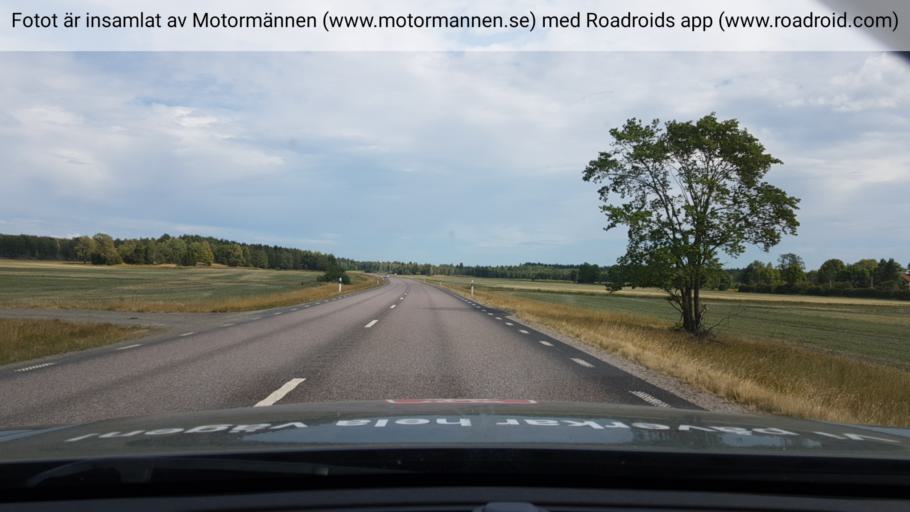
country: SE
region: Uppsala
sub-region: Enkopings Kommun
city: Orsundsbro
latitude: 59.8737
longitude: 17.2956
